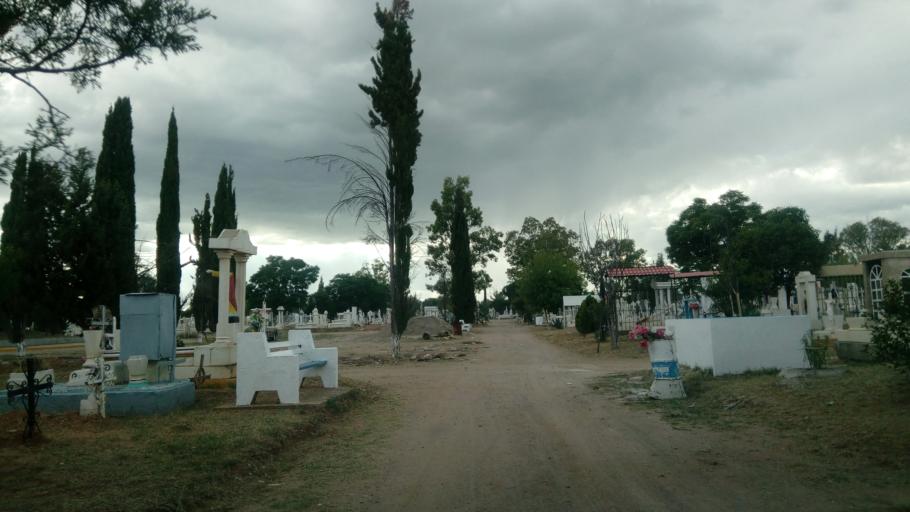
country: MX
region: Durango
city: Victoria de Durango
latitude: 24.0293
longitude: -104.6375
